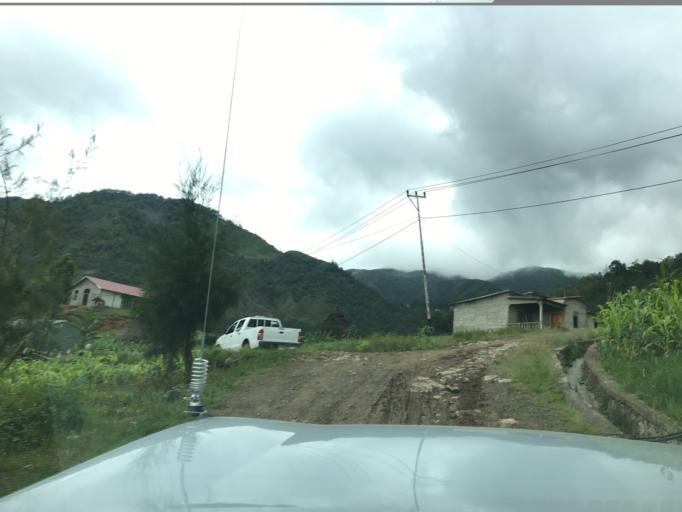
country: TL
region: Aileu
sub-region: Aileu Villa
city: Aileu
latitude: -8.8601
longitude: 125.5668
